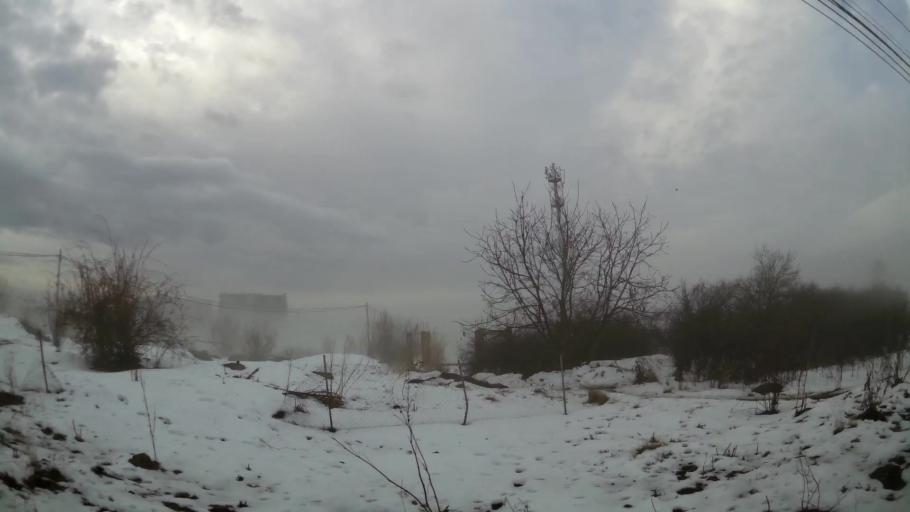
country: XK
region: Pristina
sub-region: Komuna e Prishtines
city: Pristina
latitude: 42.6608
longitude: 21.1467
